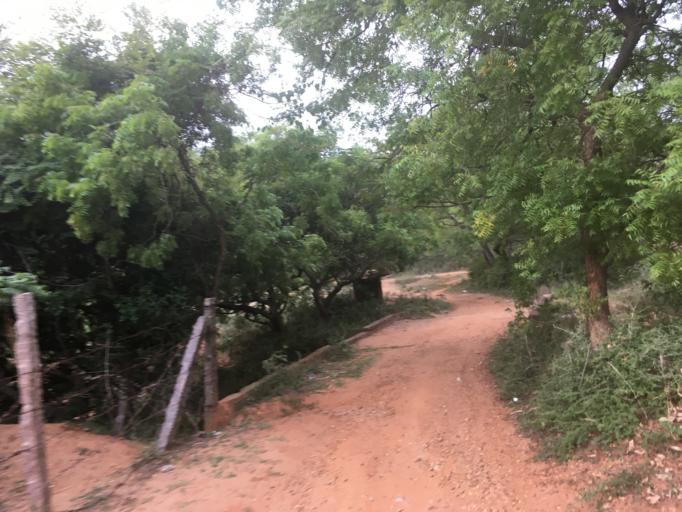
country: IN
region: Tamil Nadu
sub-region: Villupuram
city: Auroville
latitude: 12.0096
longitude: 79.8040
